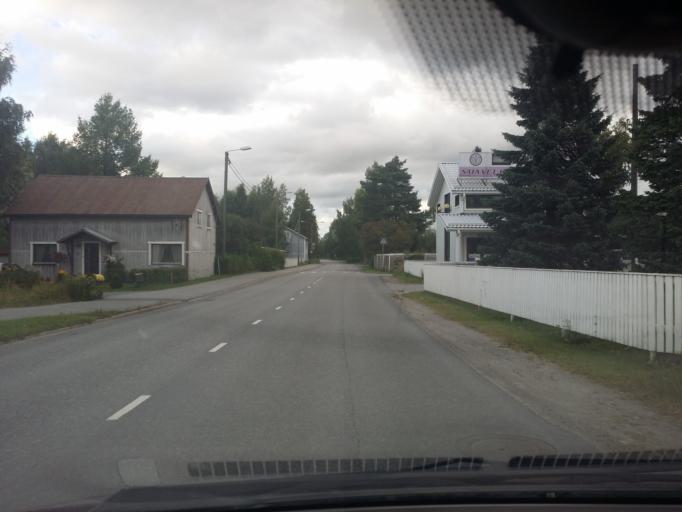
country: FI
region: Satakunta
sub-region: Pori
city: Pori
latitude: 61.4993
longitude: 21.8040
